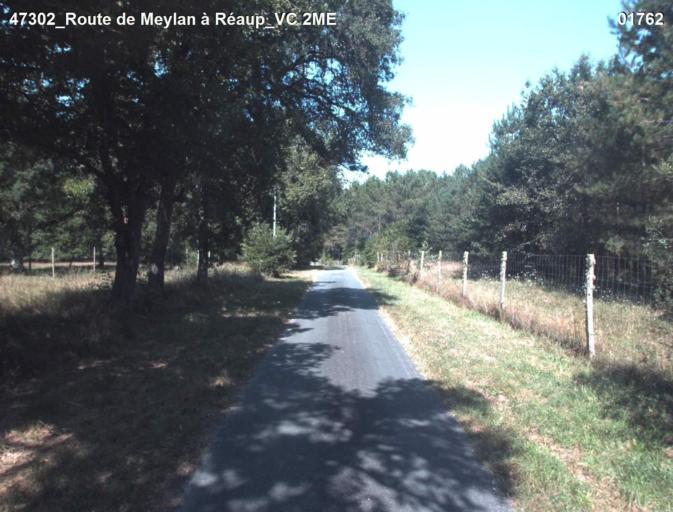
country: FR
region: Aquitaine
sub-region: Departement du Lot-et-Garonne
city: Mezin
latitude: 44.0937
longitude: 0.1307
